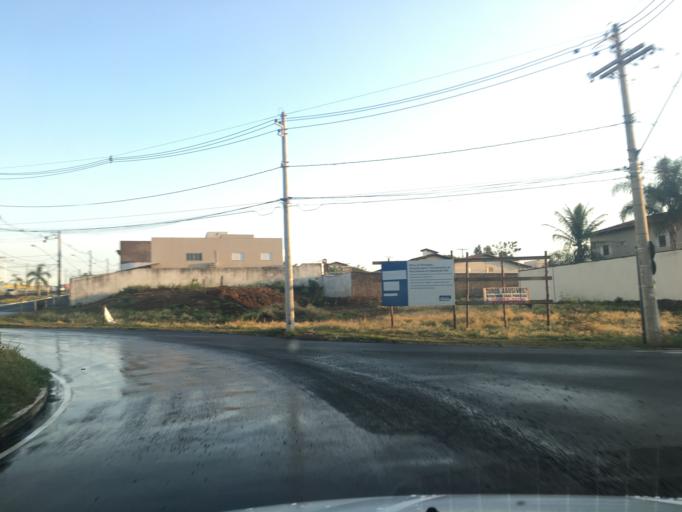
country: BR
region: Minas Gerais
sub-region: Uberlandia
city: Uberlandia
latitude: -18.9341
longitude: -48.2617
